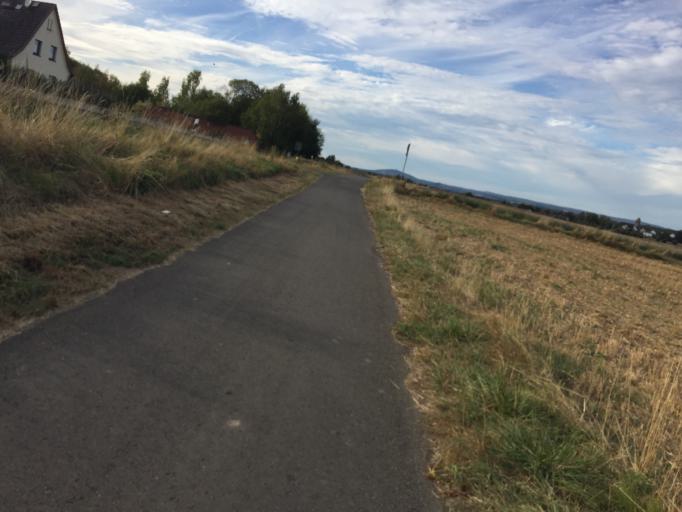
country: DE
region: Hesse
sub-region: Regierungsbezirk Giessen
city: Langgons
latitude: 50.5232
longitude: 8.7194
